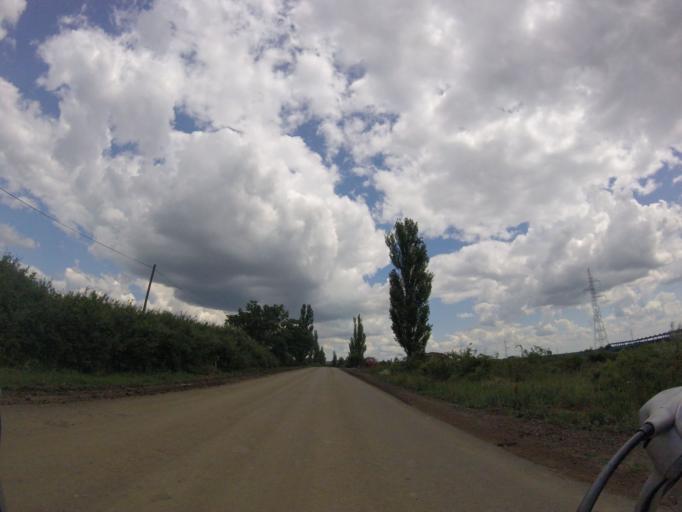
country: HU
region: Heves
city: Domoszlo
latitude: 47.7738
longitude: 20.1294
